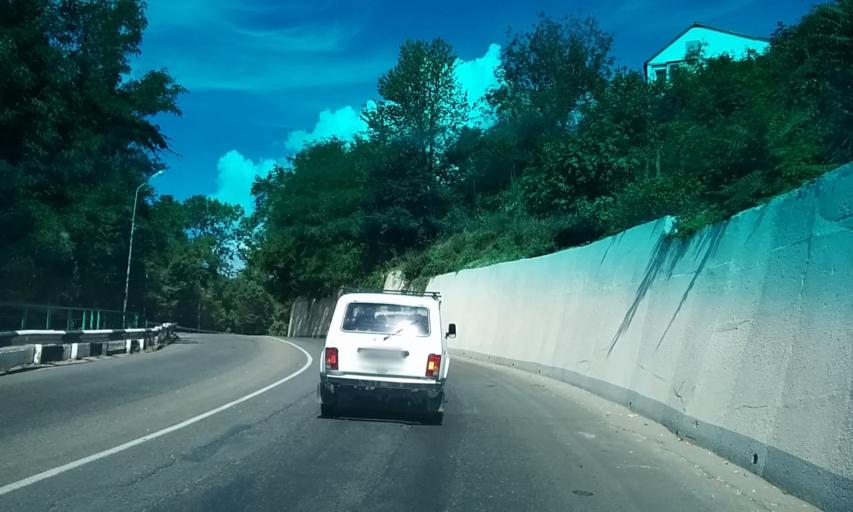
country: RU
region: Krasnodarskiy
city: Tuapse
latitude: 44.1023
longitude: 39.0645
